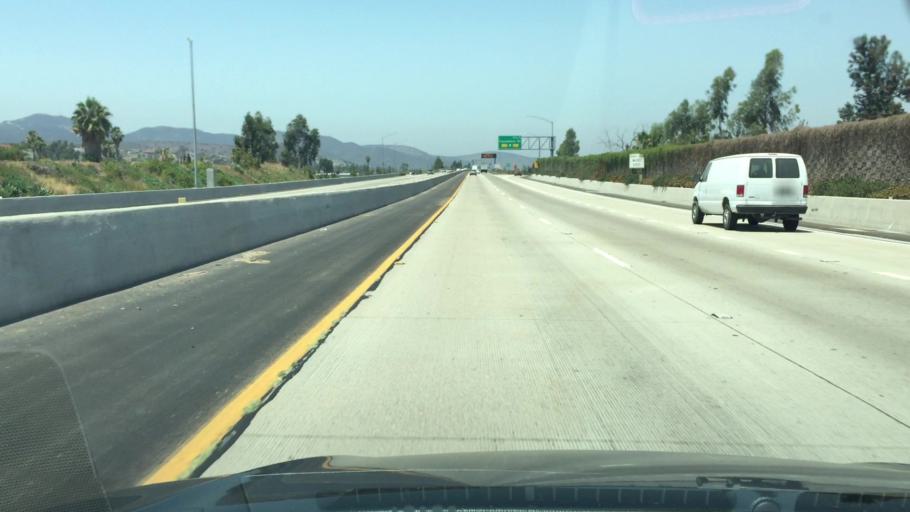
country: US
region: California
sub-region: San Diego County
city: Santee
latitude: 32.8329
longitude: -116.9772
